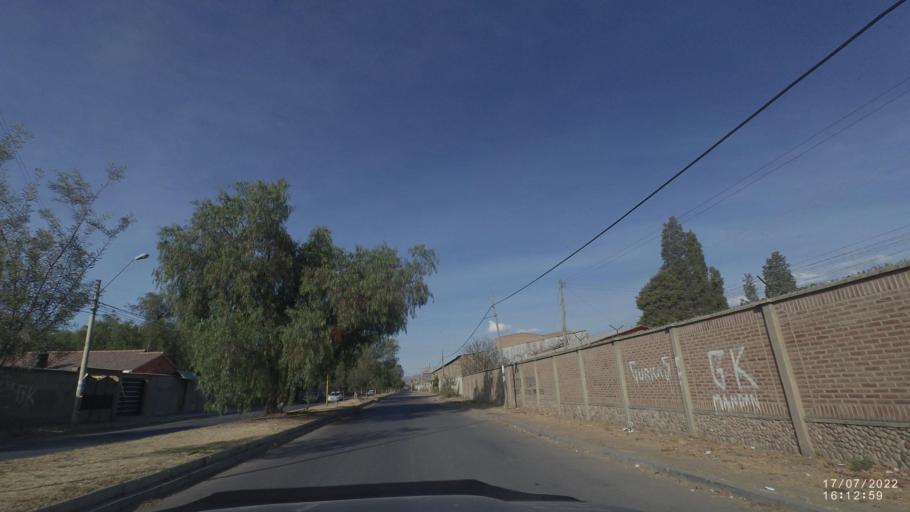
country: BO
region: Cochabamba
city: Cochabamba
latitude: -17.3934
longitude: -66.2580
